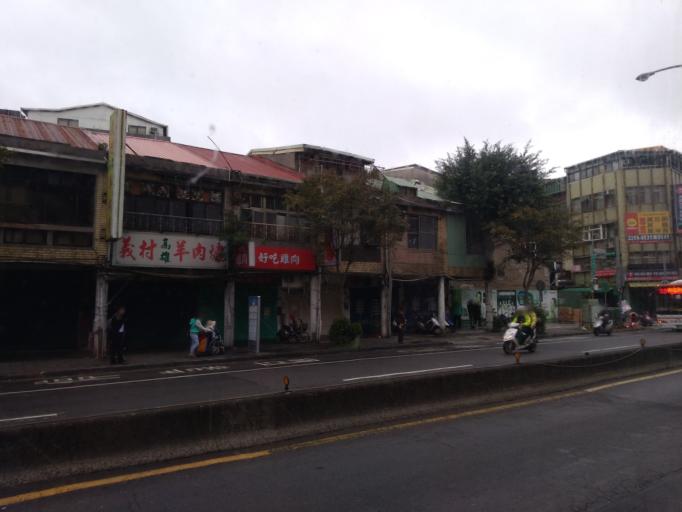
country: TW
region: Taipei
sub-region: Taipei
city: Banqiao
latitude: 25.0239
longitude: 121.5001
